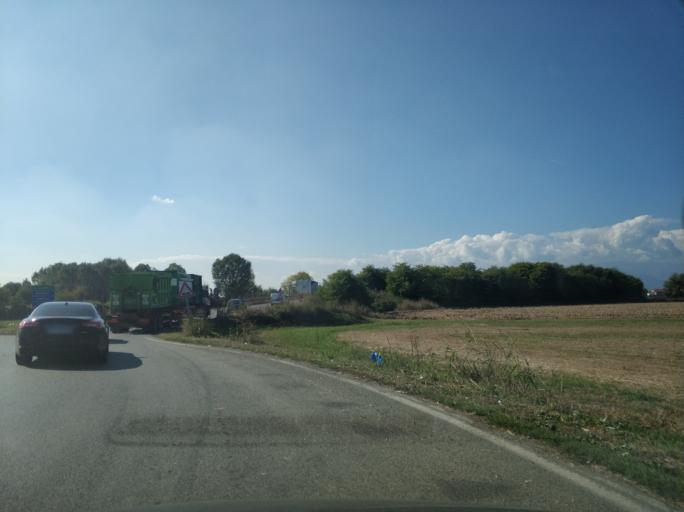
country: IT
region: Piedmont
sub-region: Provincia di Torino
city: Borgaro Torinese
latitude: 45.1396
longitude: 7.6971
